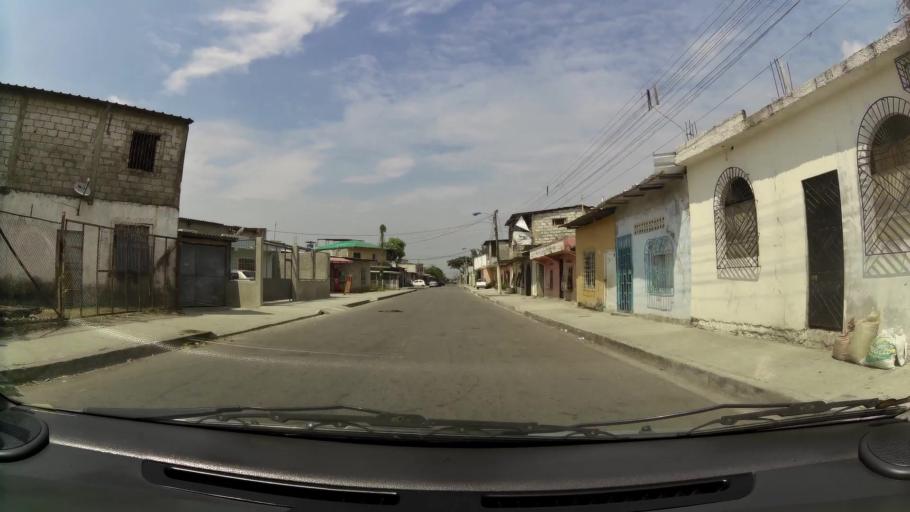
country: EC
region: Guayas
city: Guayaquil
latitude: -2.2630
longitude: -79.8740
